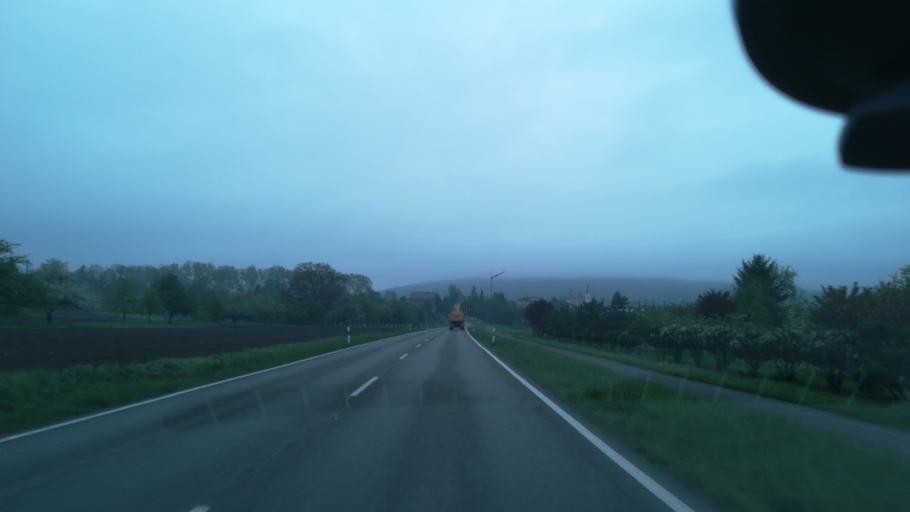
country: DE
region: Baden-Wuerttemberg
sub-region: Freiburg Region
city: Steisslingen
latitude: 47.7909
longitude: 8.9189
